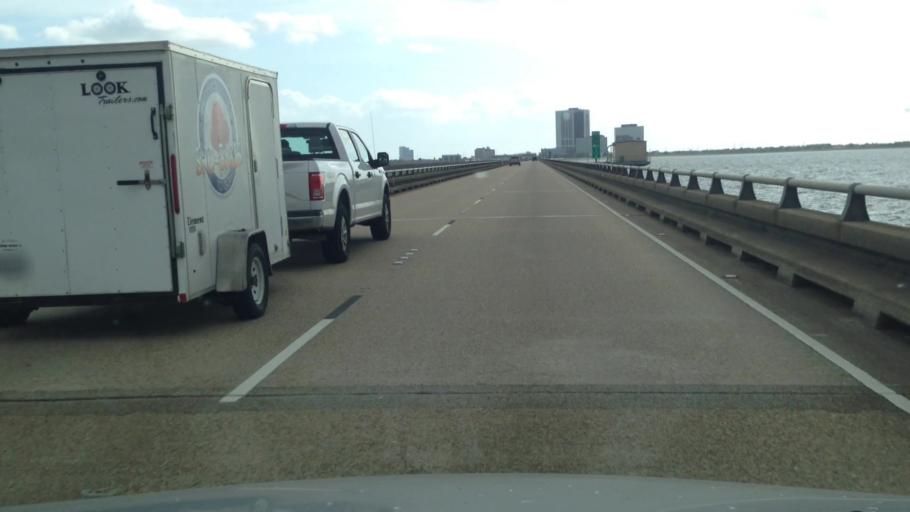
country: US
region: Louisiana
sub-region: Jefferson Parish
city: Metairie
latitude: 30.0394
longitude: -90.1510
